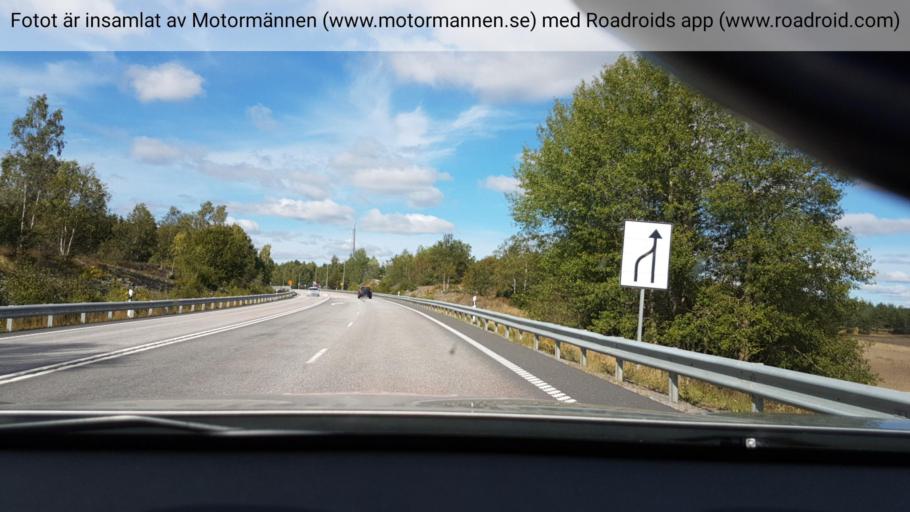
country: SE
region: Stockholm
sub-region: Osterakers Kommun
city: Akersberga
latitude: 59.4467
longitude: 18.2206
